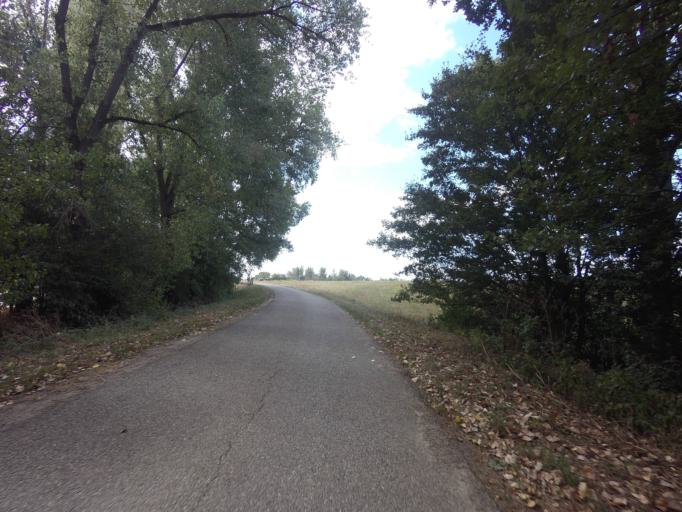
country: NL
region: North Brabant
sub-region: Gemeente Oss
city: Berghem
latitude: 51.8111
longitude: 5.5952
